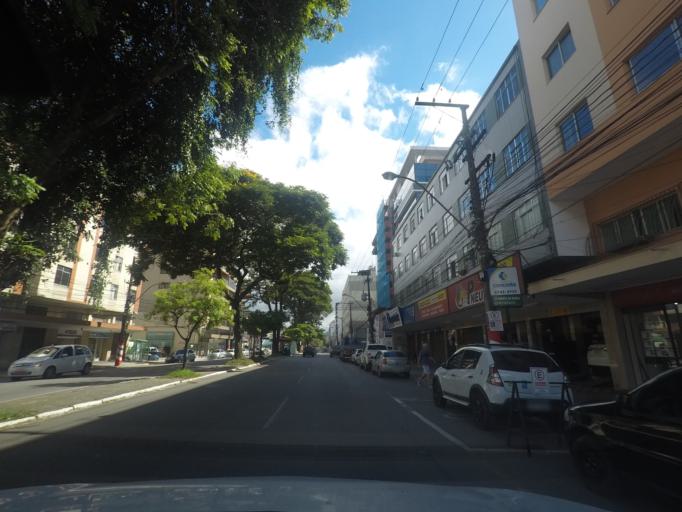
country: BR
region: Rio de Janeiro
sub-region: Teresopolis
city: Teresopolis
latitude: -22.4217
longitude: -42.9761
